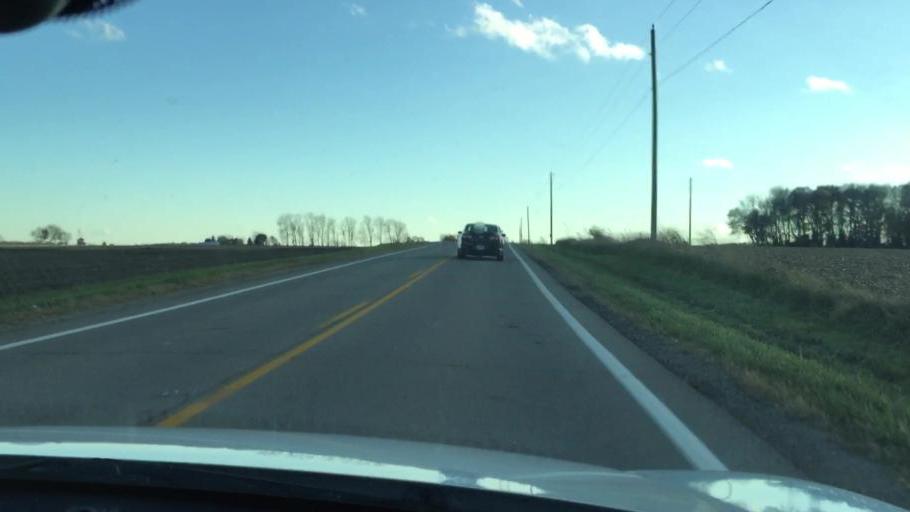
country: US
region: Ohio
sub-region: Champaign County
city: North Lewisburg
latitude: 40.1586
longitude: -83.5275
